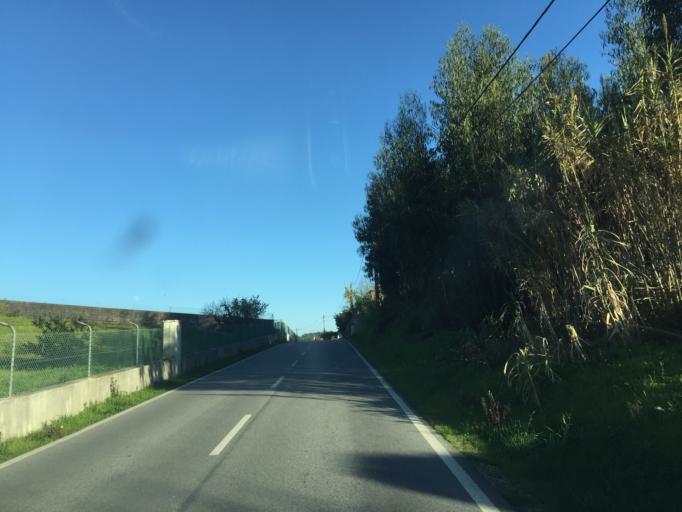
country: PT
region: Coimbra
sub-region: Figueira da Foz
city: Tavarede
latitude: 40.1658
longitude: -8.8236
